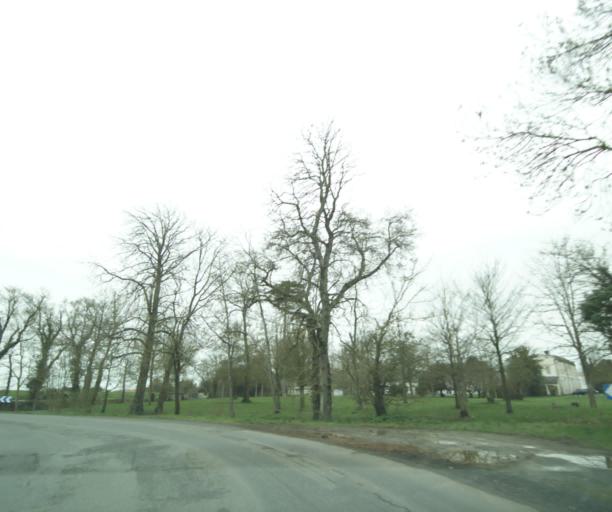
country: FR
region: Poitou-Charentes
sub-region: Departement de la Charente-Maritime
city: Lagord
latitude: 46.1900
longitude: -1.1376
